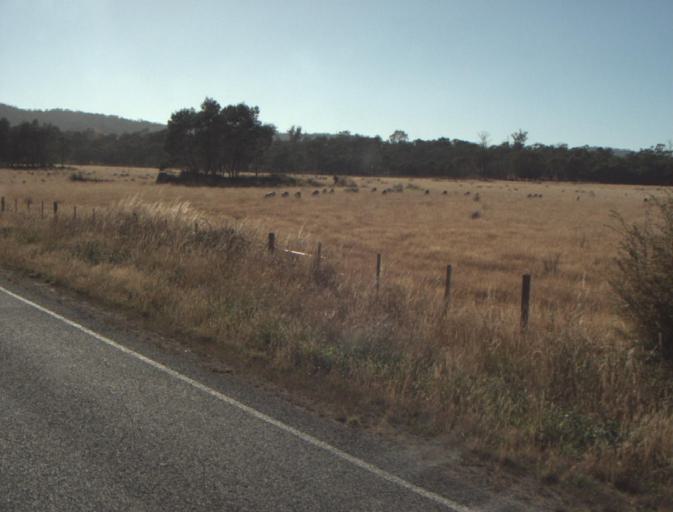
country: AU
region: Tasmania
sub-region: Launceston
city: Newstead
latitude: -41.4464
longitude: 147.2491
